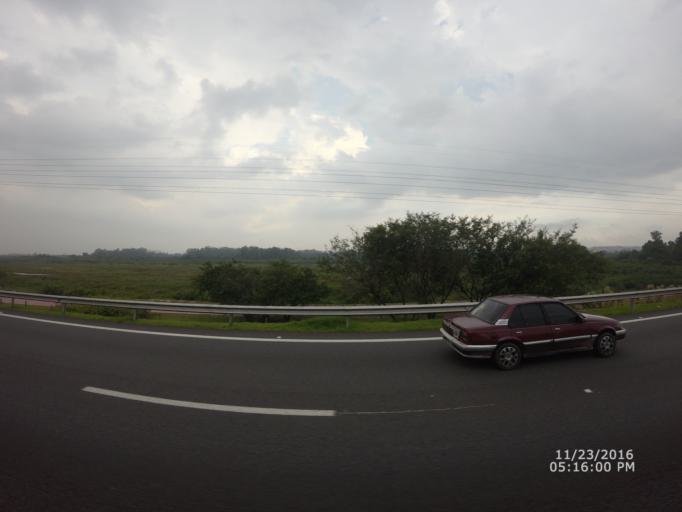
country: BR
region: Sao Paulo
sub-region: Guarulhos
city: Guarulhos
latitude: -23.4852
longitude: -46.5289
